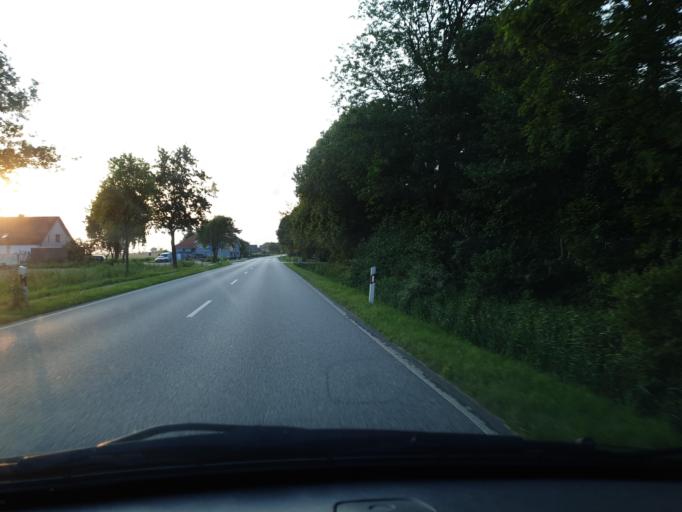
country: DE
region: Schleswig-Holstein
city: Schmedeswurth
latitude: 53.9252
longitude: 9.0415
